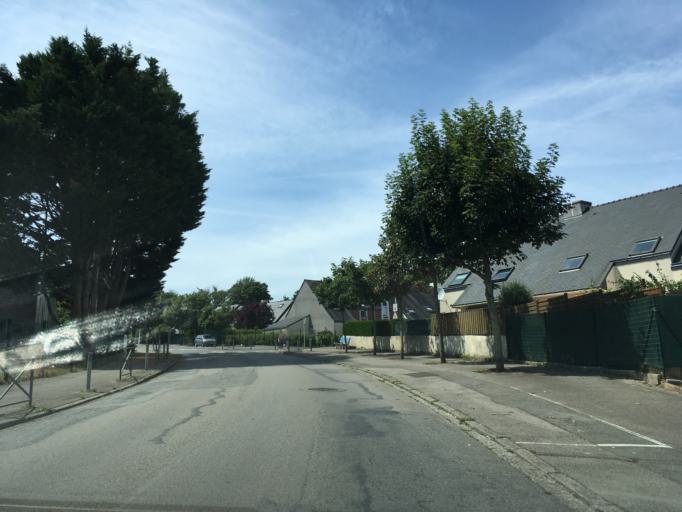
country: FR
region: Brittany
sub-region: Departement du Morbihan
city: Lorient
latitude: 47.7469
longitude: -3.3816
